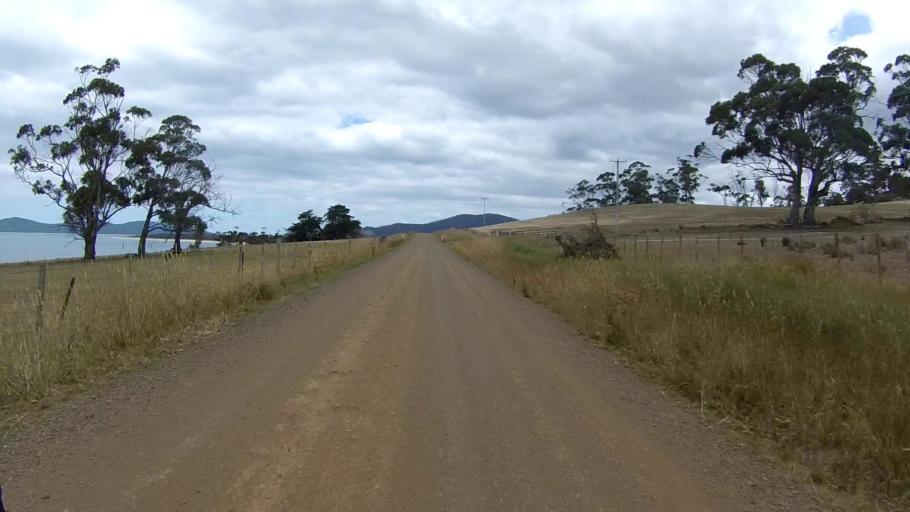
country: AU
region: Tasmania
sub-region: Sorell
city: Sorell
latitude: -42.6240
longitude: 147.9329
